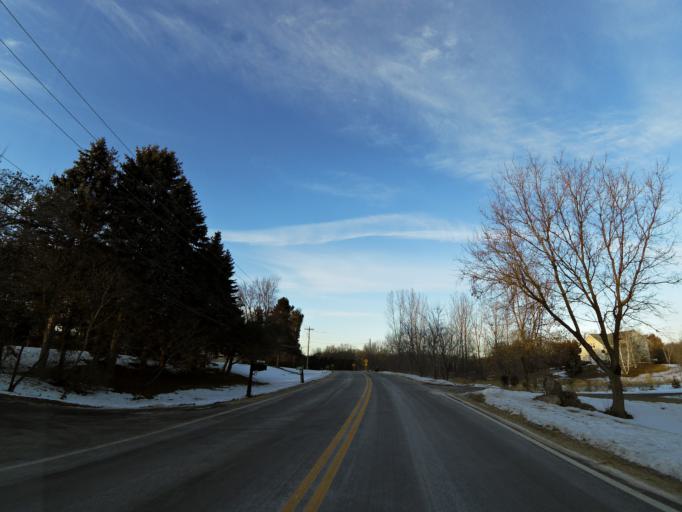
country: US
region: Minnesota
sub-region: Washington County
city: Lake Elmo
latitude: 44.9806
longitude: -92.8629
